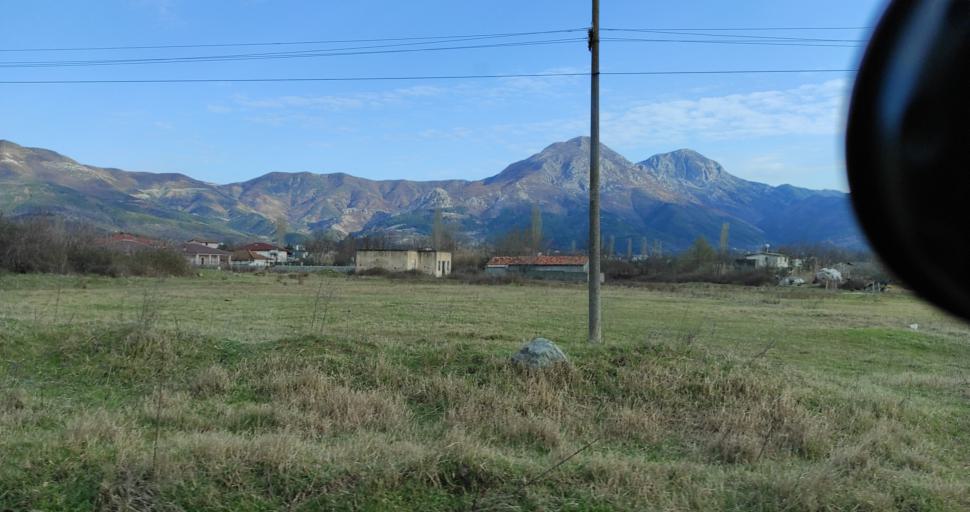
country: AL
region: Lezhe
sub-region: Rrethi i Lezhes
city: Kallmeti i Madh
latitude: 41.8791
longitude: 19.6753
